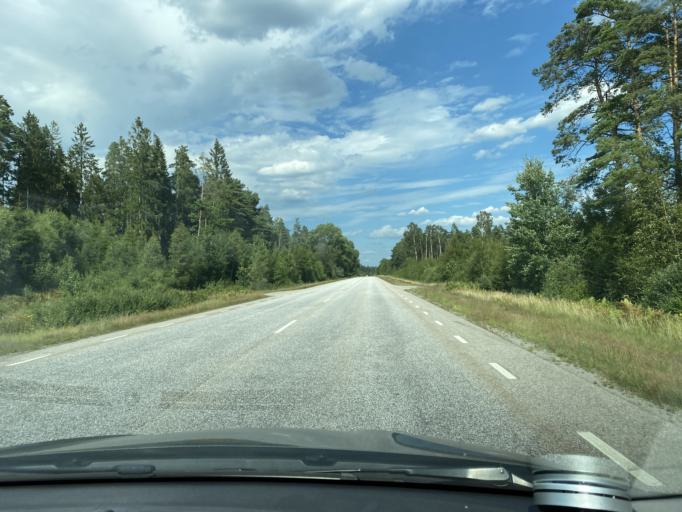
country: SE
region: Kronoberg
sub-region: Markaryds Kommun
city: Markaryd
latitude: 56.4163
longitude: 13.5439
